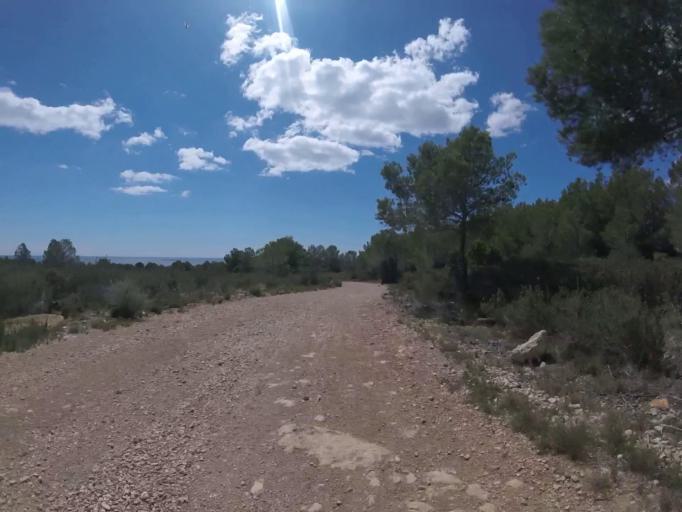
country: ES
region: Valencia
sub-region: Provincia de Castello
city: Alcoceber
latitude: 40.2870
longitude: 0.3198
